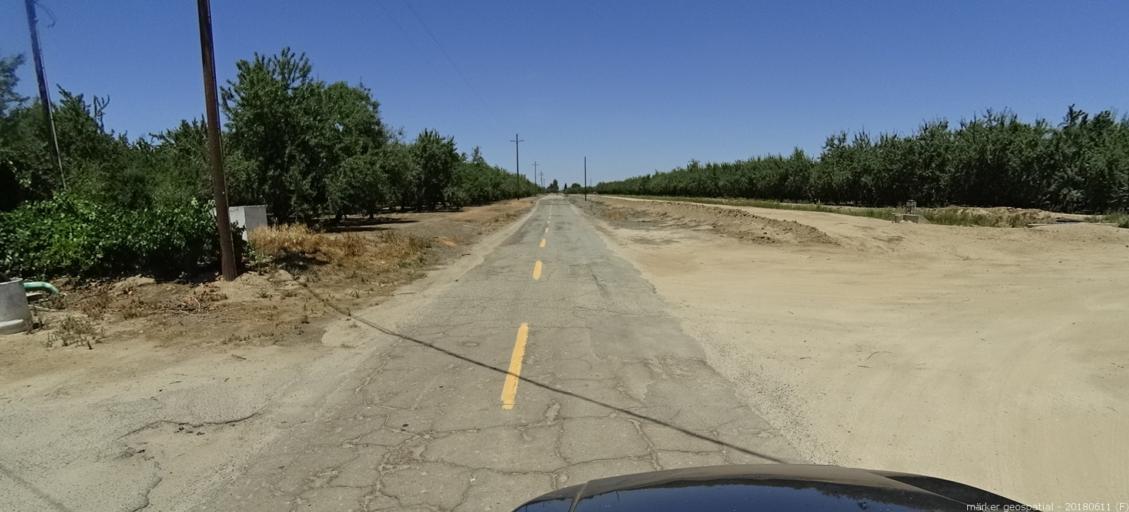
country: US
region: California
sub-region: Madera County
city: Fairmead
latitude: 37.0509
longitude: -120.1934
